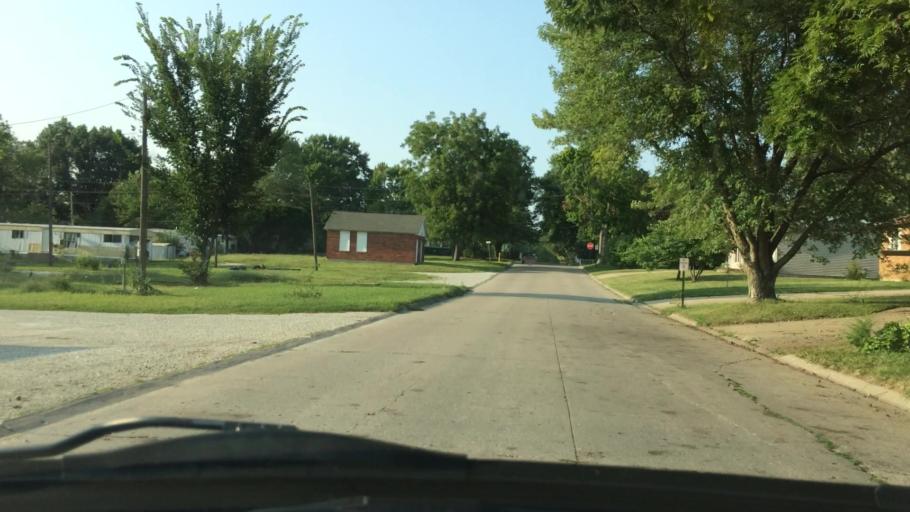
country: US
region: Iowa
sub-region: Henry County
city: Mount Pleasant
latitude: 40.9662
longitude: -91.5602
